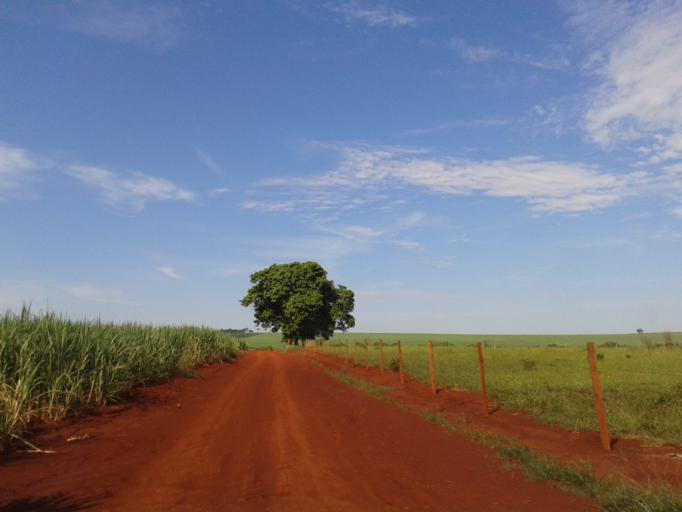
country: BR
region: Minas Gerais
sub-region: Centralina
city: Centralina
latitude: -18.6350
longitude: -49.2511
